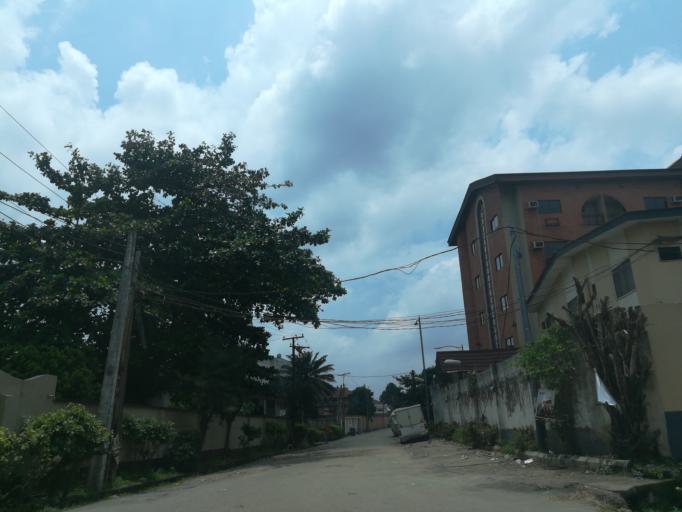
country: NG
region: Lagos
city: Ikeja
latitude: 6.5960
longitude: 3.3587
